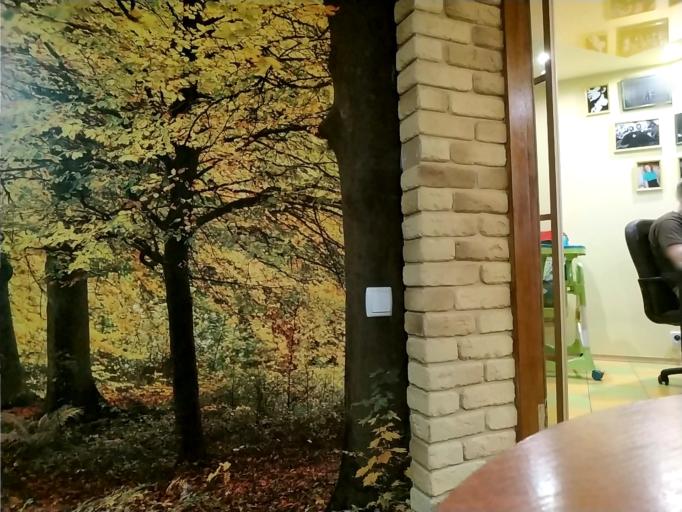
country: RU
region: Tverskaya
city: Zapadnaya Dvina
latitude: 56.3329
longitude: 31.8806
